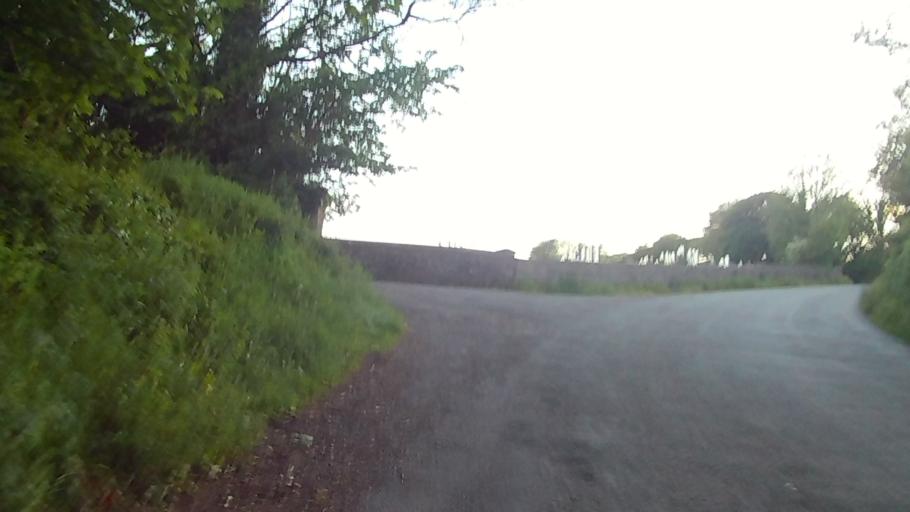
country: IE
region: Munster
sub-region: County Cork
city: Carrigtwohill
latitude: 51.9723
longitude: -8.2296
